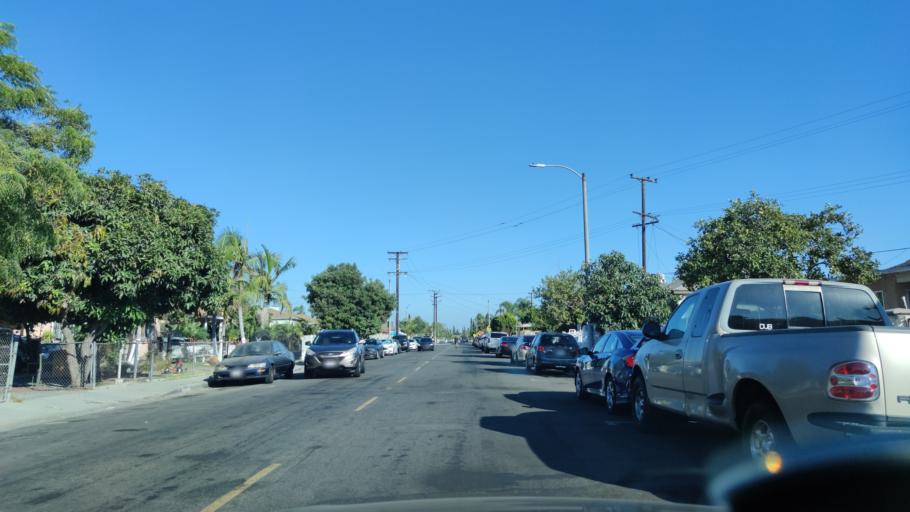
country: US
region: California
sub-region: Los Angeles County
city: Maywood
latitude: 33.9929
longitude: -118.1862
